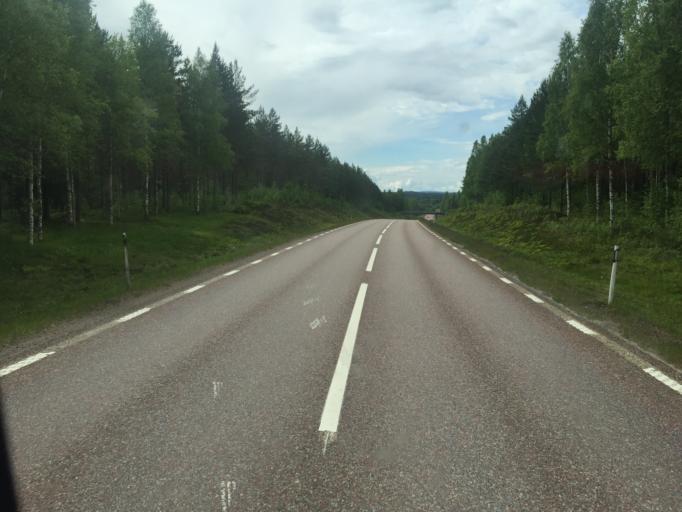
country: SE
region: Dalarna
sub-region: Vansbro Kommun
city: Vansbro
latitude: 60.4764
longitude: 14.1027
